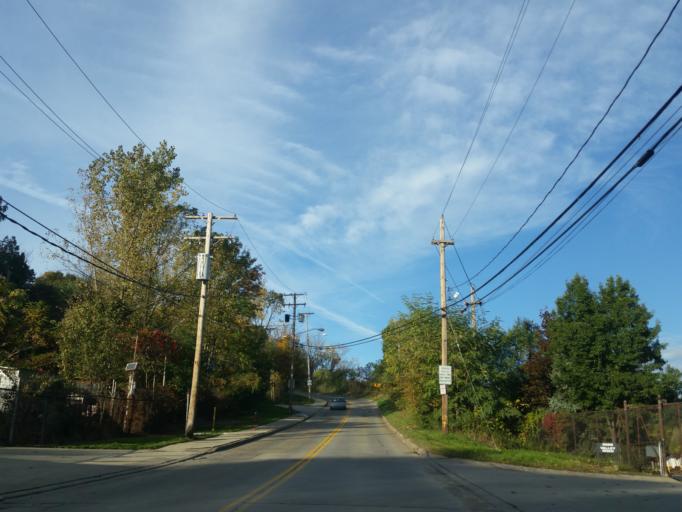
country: US
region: Ohio
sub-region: Cuyahoga County
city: Brooklyn Heights
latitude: 41.4460
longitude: -81.6918
